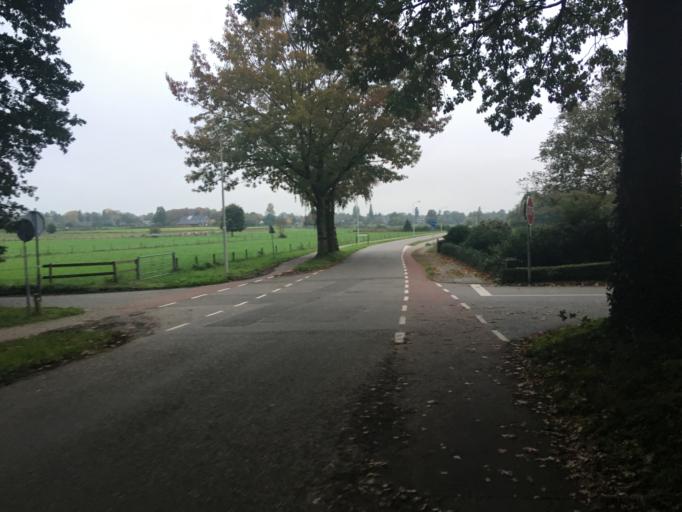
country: NL
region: Gelderland
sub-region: Gemeente Wageningen
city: Wageningen
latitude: 51.9763
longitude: 5.6929
